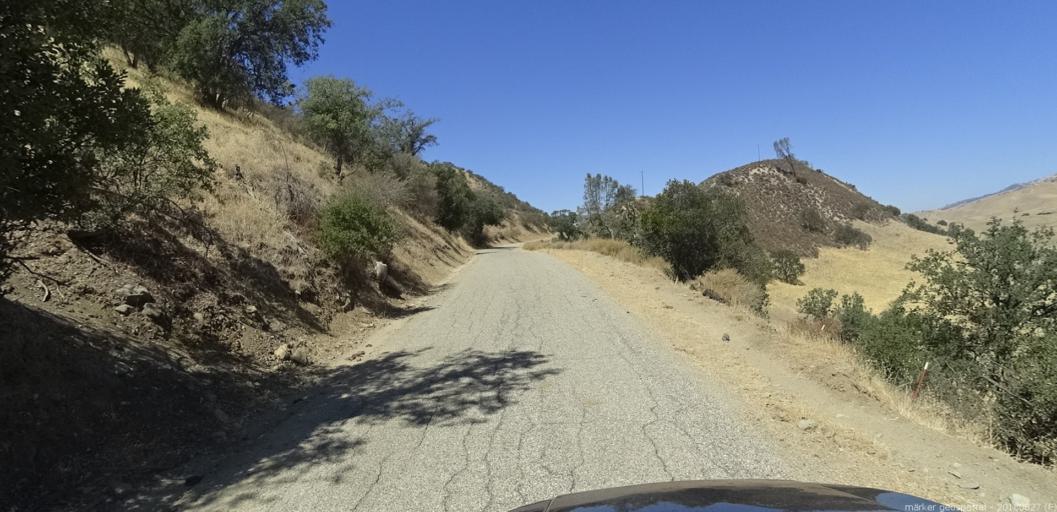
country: US
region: California
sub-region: Monterey County
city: King City
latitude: 36.2942
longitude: -120.8950
